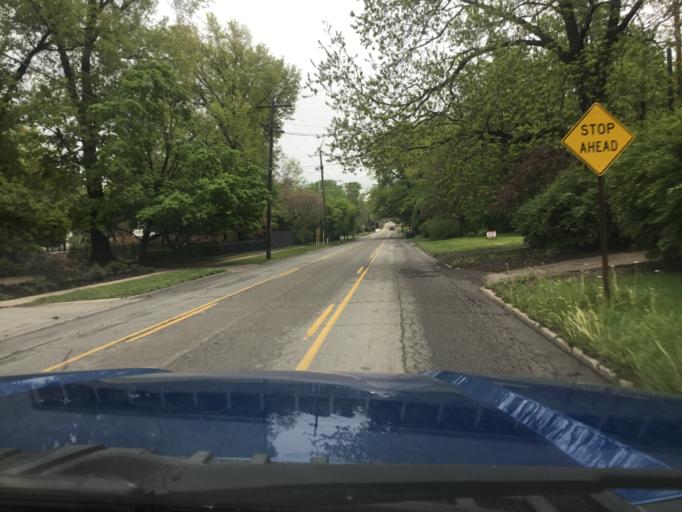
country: US
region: Kansas
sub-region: Shawnee County
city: Topeka
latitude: 39.0369
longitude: -95.7174
